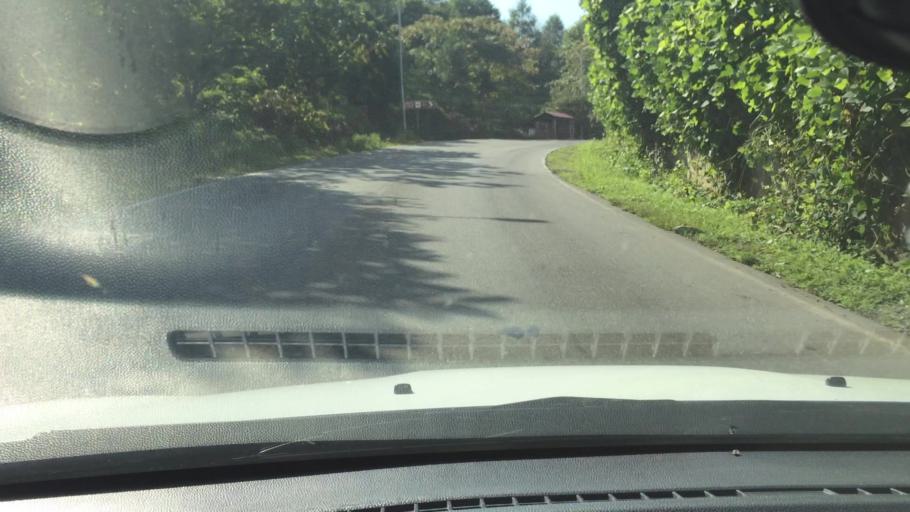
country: GE
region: Ajaria
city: Kobuleti
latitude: 41.7681
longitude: 41.7546
